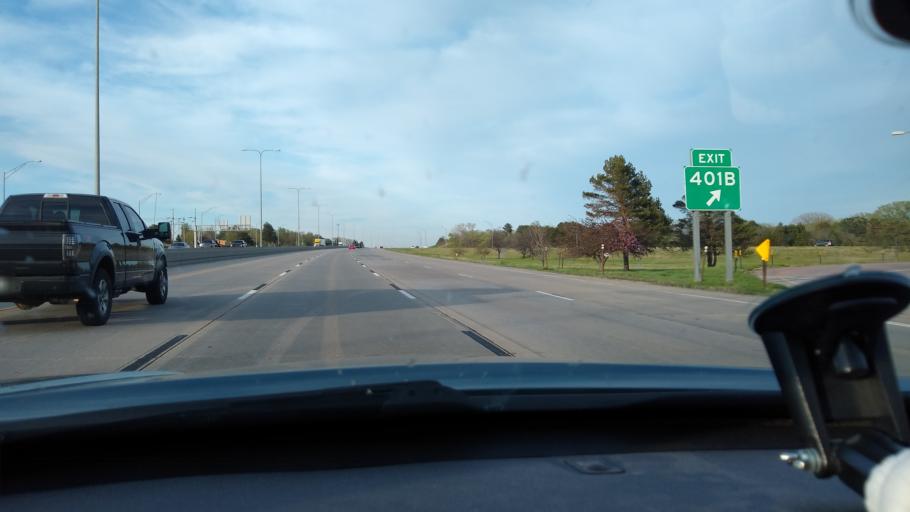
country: US
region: Nebraska
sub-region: Lancaster County
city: Lincoln
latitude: 40.8625
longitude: -96.7153
